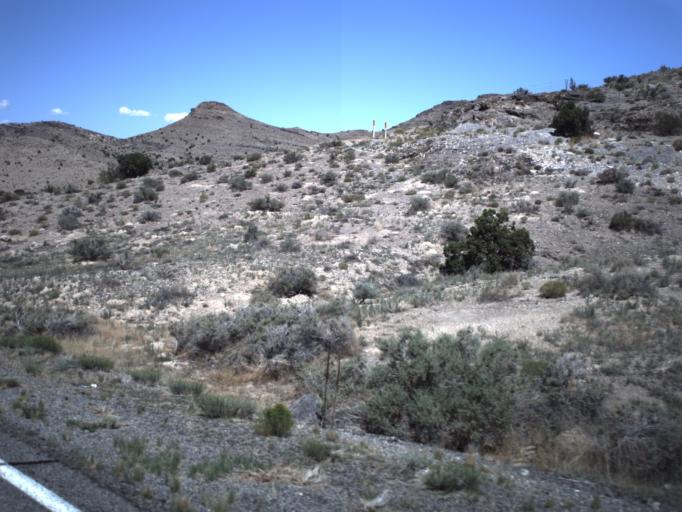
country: US
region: Utah
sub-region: Beaver County
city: Milford
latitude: 39.0792
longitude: -113.6992
